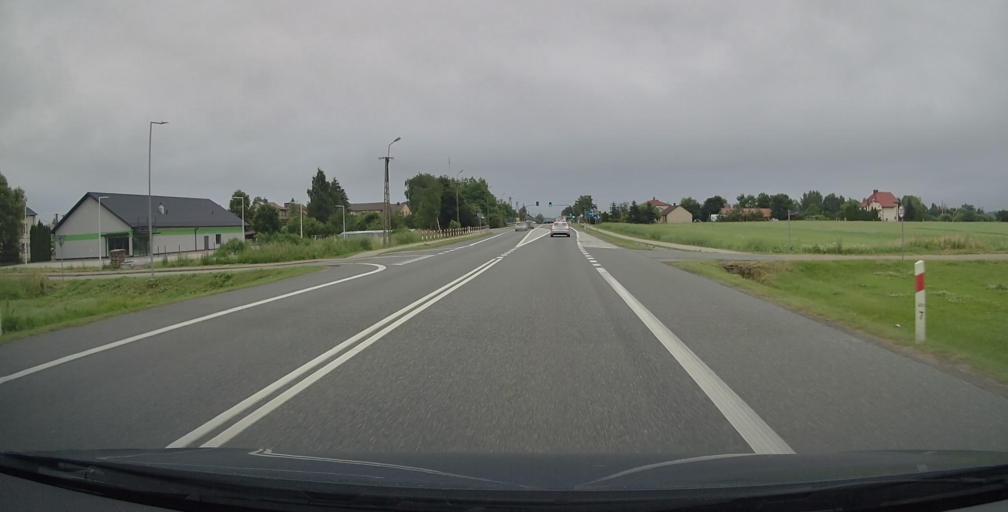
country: PL
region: Lublin Voivodeship
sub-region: Powiat bialski
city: Zalesie
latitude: 52.0355
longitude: 23.3596
